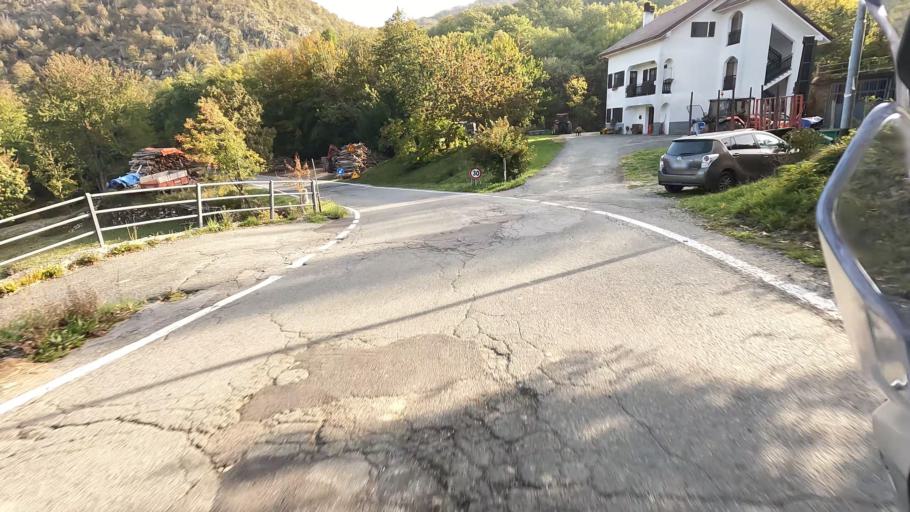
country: IT
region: Liguria
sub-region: Provincia di Savona
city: Urbe
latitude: 44.4587
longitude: 8.5550
